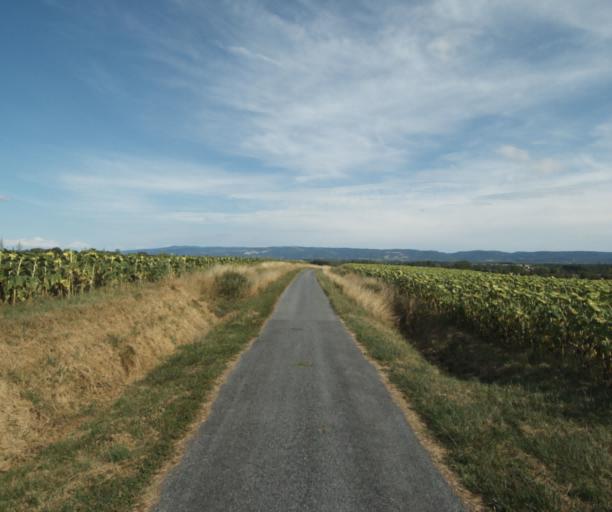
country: FR
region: Midi-Pyrenees
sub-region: Departement du Tarn
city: Puylaurens
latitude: 43.5302
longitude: 1.9915
